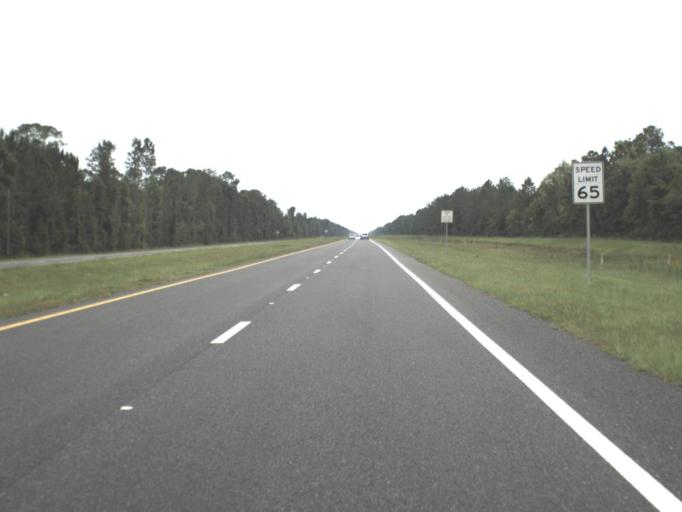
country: US
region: Florida
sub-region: Levy County
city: Chiefland
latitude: 29.3357
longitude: -82.7735
